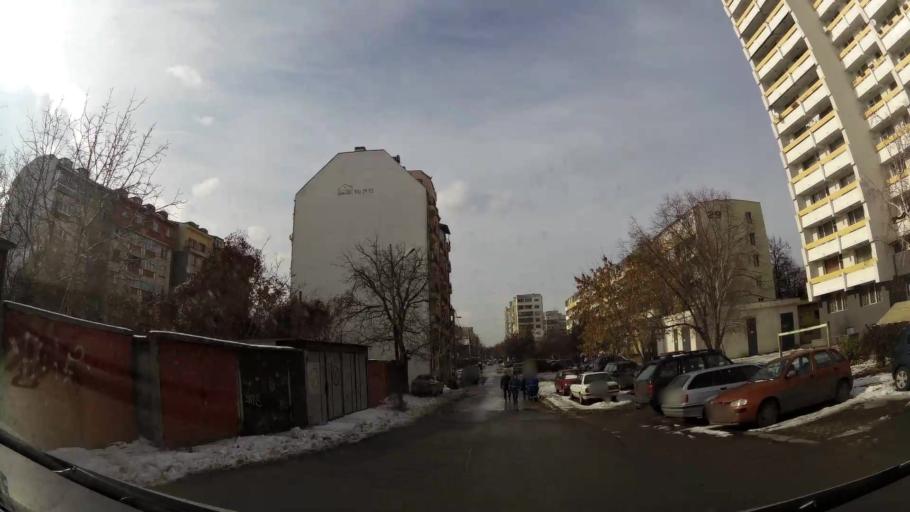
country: BG
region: Sofia-Capital
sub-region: Stolichna Obshtina
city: Sofia
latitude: 42.7079
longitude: 23.3630
